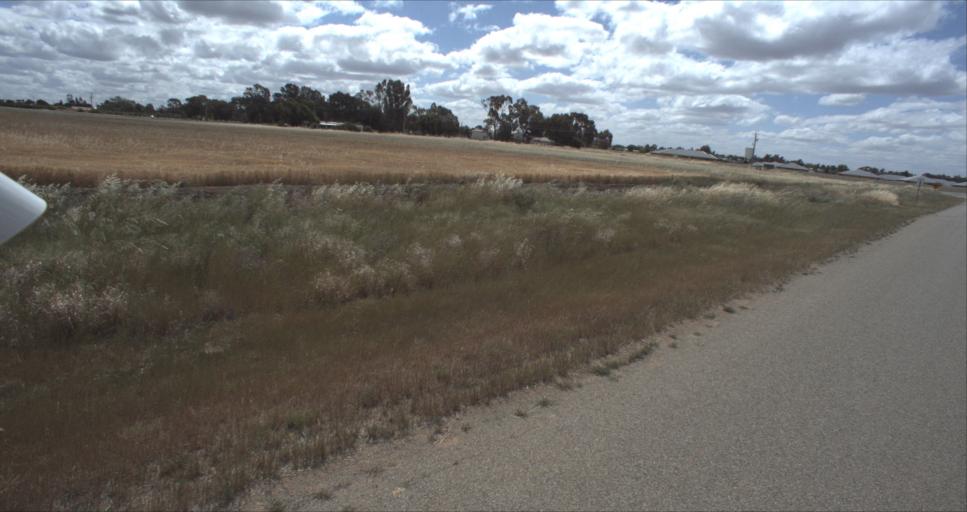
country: AU
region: New South Wales
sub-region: Leeton
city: Leeton
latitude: -34.5729
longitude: 146.3988
